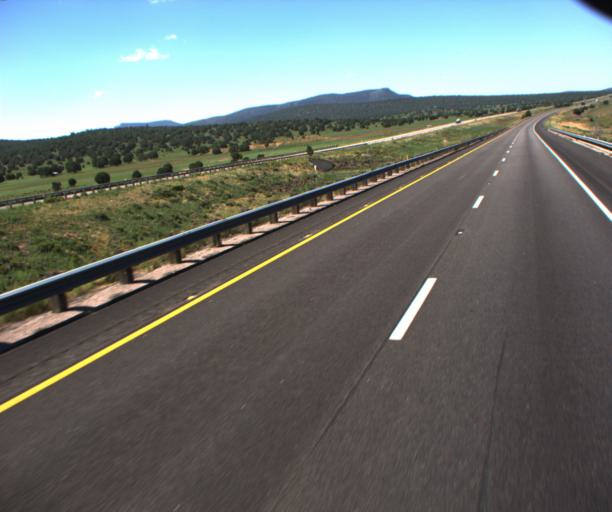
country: US
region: Arizona
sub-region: Mohave County
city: Peach Springs
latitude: 35.2369
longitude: -113.2075
